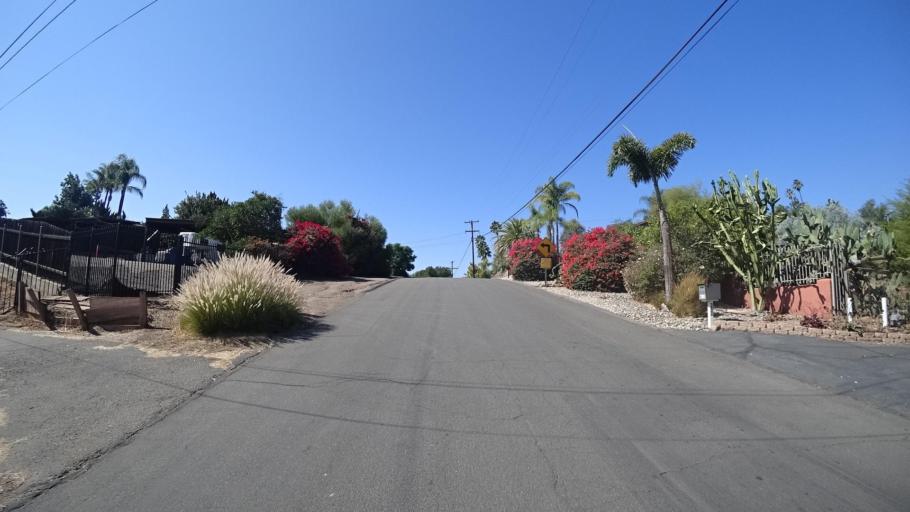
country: US
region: California
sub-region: San Diego County
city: Granite Hills
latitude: 32.7916
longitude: -116.9136
